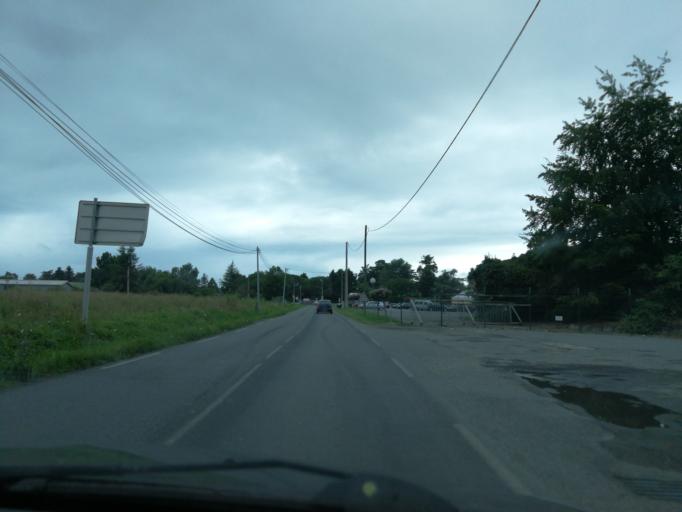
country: FR
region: Midi-Pyrenees
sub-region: Departement des Hautes-Pyrenees
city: Bazet
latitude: 43.2680
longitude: 0.0738
